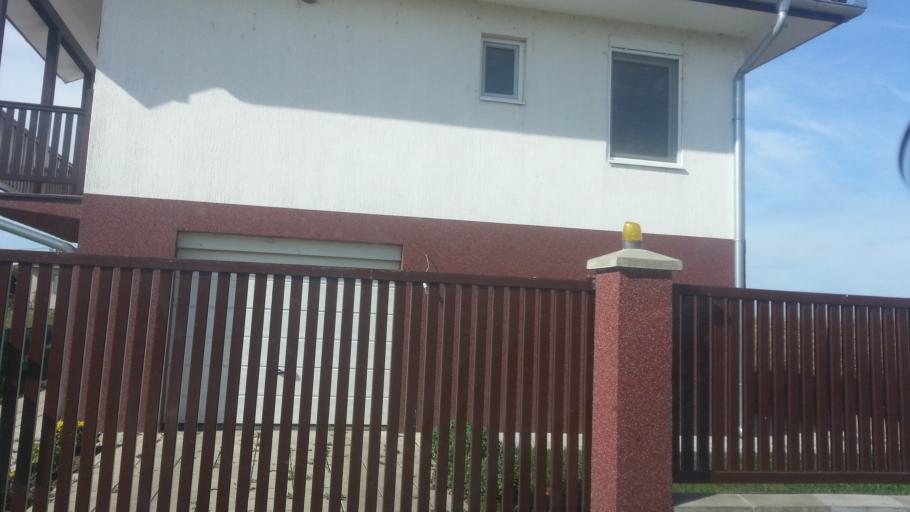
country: RS
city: Stari Banovci
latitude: 44.9712
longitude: 20.2734
